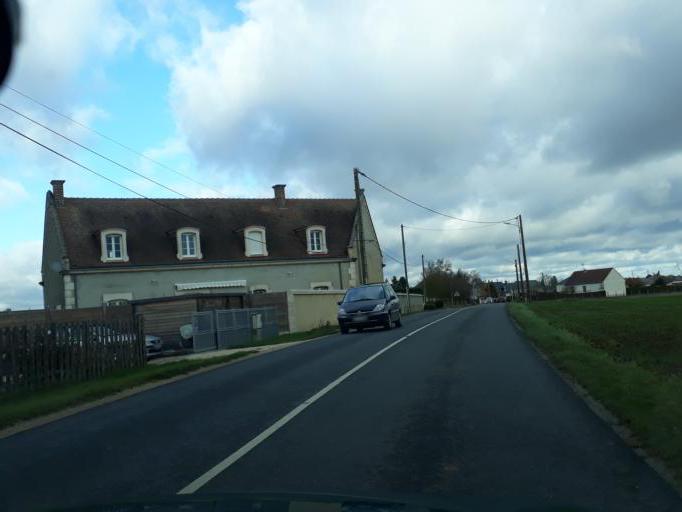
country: FR
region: Centre
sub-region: Departement du Loir-et-Cher
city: La Chaussee-Saint-Victor
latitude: 47.6574
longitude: 1.3684
